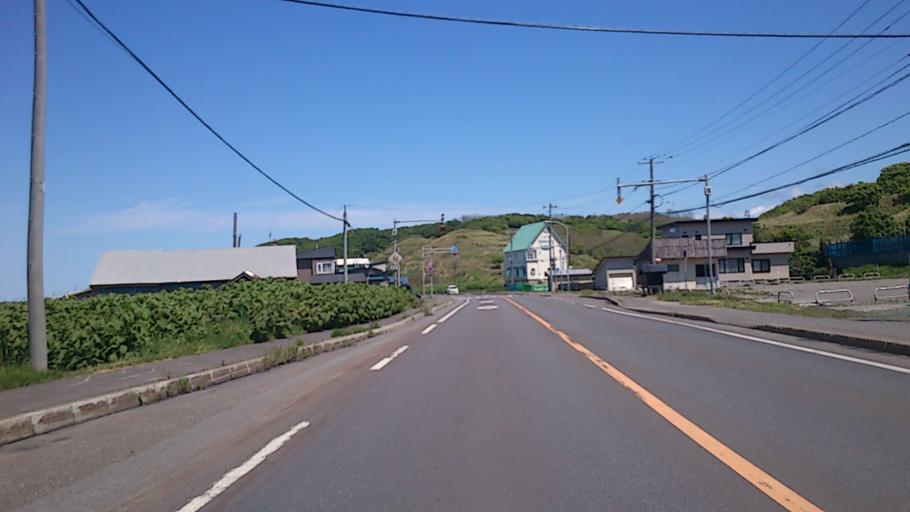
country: JP
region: Hokkaido
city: Rumoi
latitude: 43.9649
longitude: 141.6451
